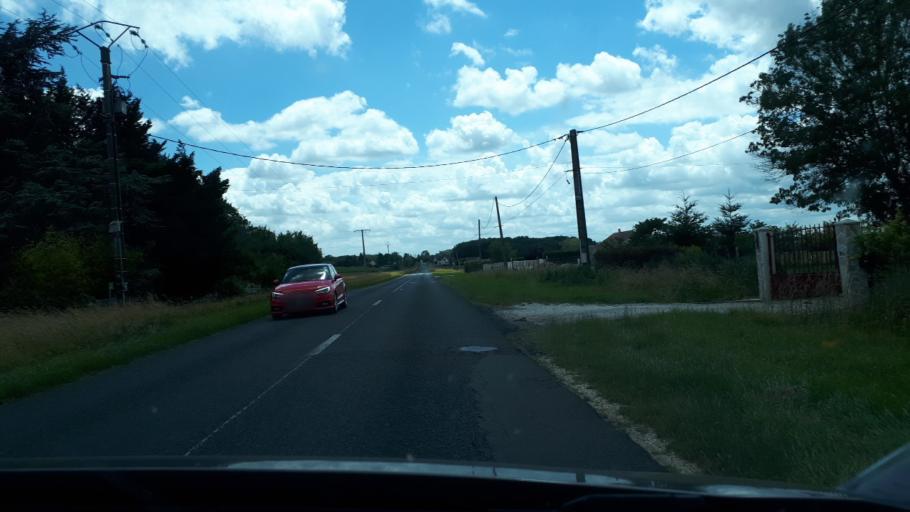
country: FR
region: Centre
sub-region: Departement du Loir-et-Cher
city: Contres
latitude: 47.3743
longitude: 1.4059
